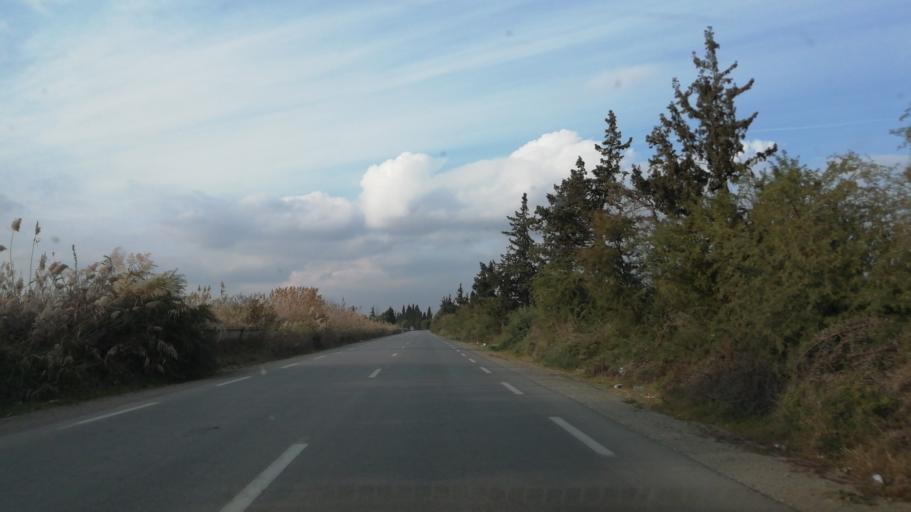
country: DZ
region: Mascara
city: Mascara
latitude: 35.6286
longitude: 0.0416
